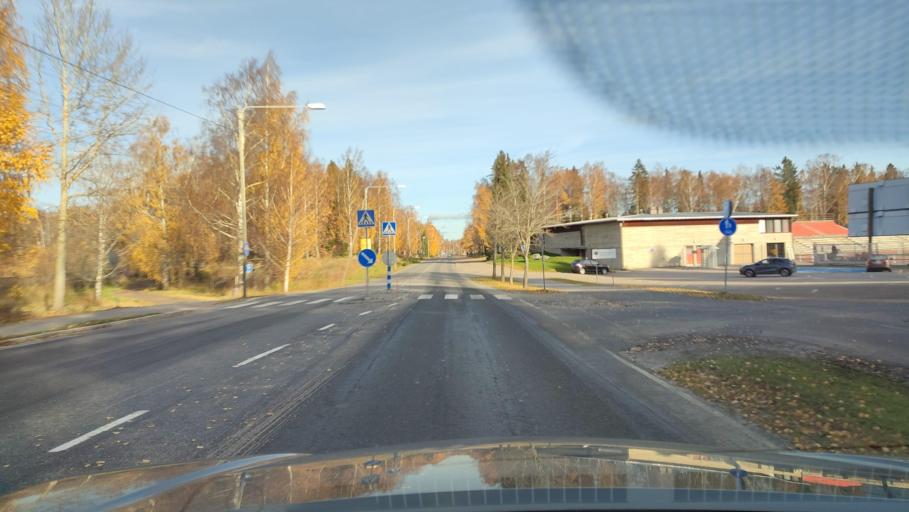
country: FI
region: Ostrobothnia
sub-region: Vaasa
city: Vaasa
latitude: 63.0829
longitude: 21.6378
